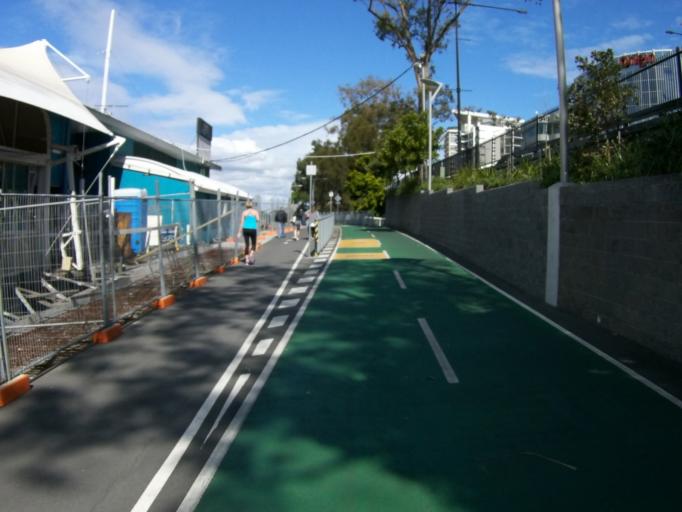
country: AU
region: Queensland
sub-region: Brisbane
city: Milton
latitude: -27.4744
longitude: 153.0041
